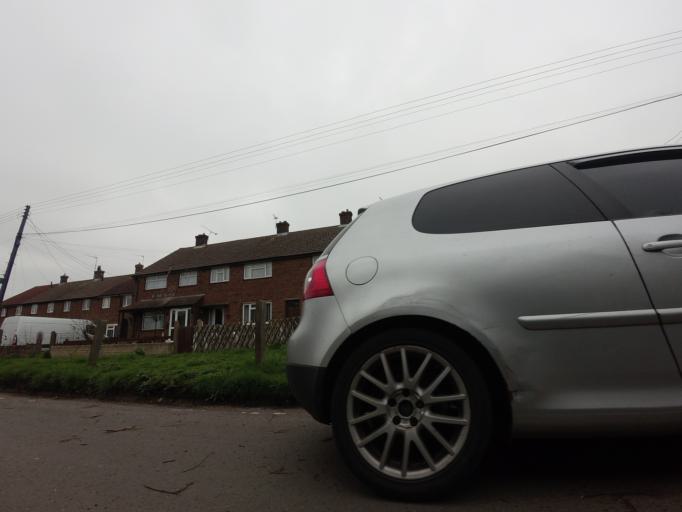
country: GB
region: England
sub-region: Kent
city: Swanley
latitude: 51.3784
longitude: 0.1605
